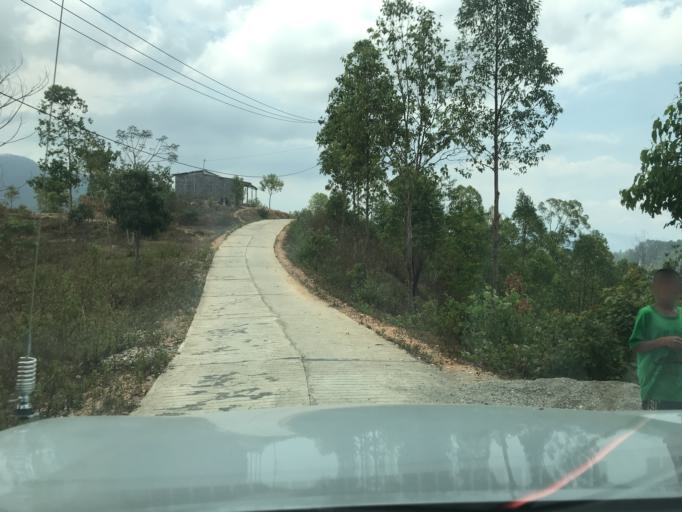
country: TL
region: Dili
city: Dili
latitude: -8.6154
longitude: 125.5698
